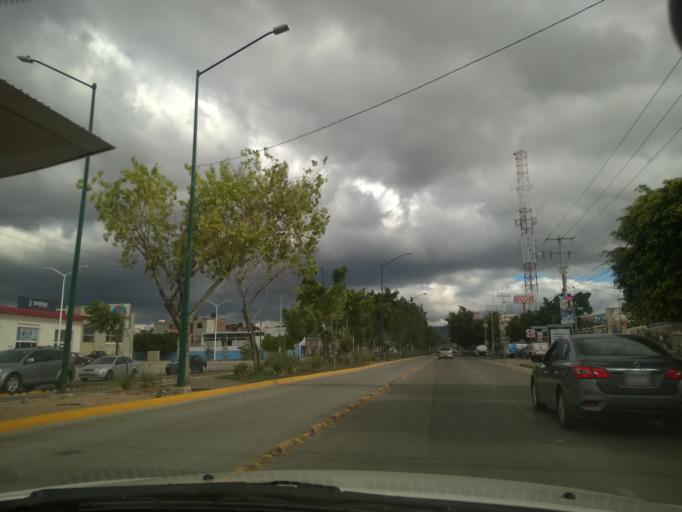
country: MX
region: Guanajuato
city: Leon
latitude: 21.1249
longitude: -101.6482
